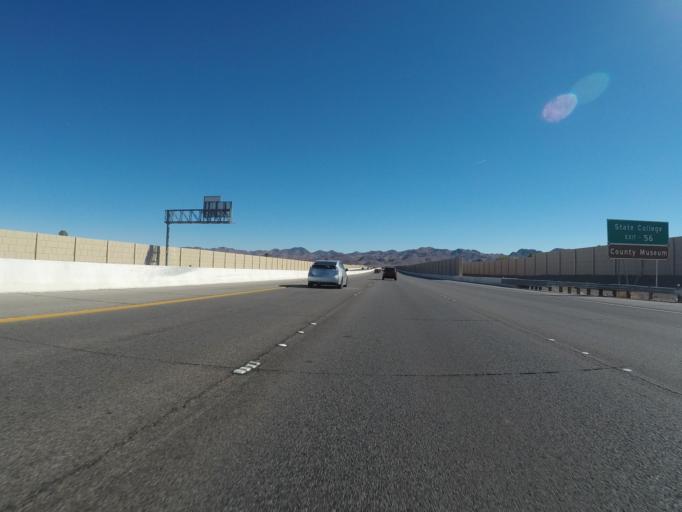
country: US
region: Nevada
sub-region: Clark County
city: Henderson
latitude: 35.9999
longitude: -114.9569
